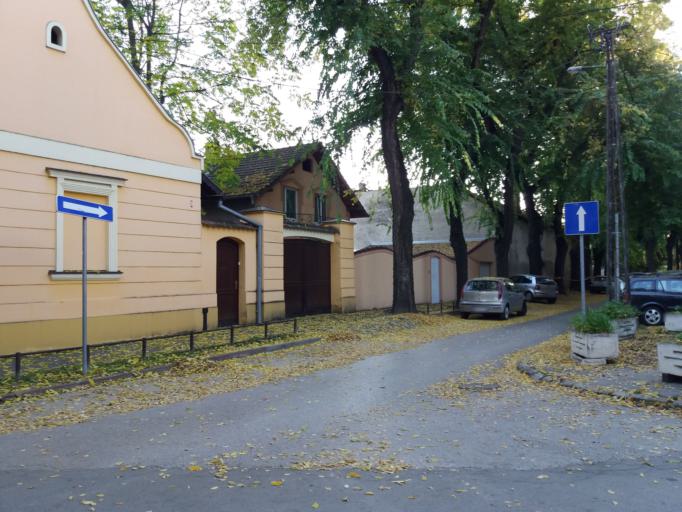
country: RS
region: Autonomna Pokrajina Vojvodina
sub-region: Severnobacki Okrug
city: Subotica
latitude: 46.0983
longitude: 19.6579
